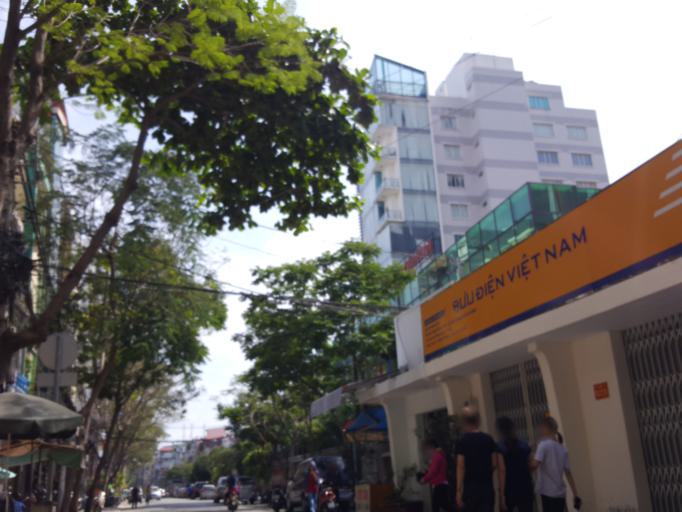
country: VN
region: Ho Chi Minh City
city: Quan Bon
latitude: 10.7649
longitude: 106.7034
